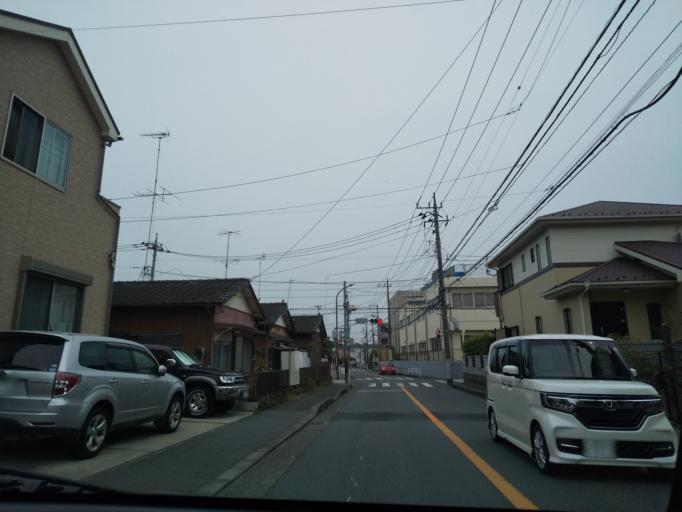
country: JP
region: Kanagawa
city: Zama
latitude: 35.5057
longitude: 139.4044
